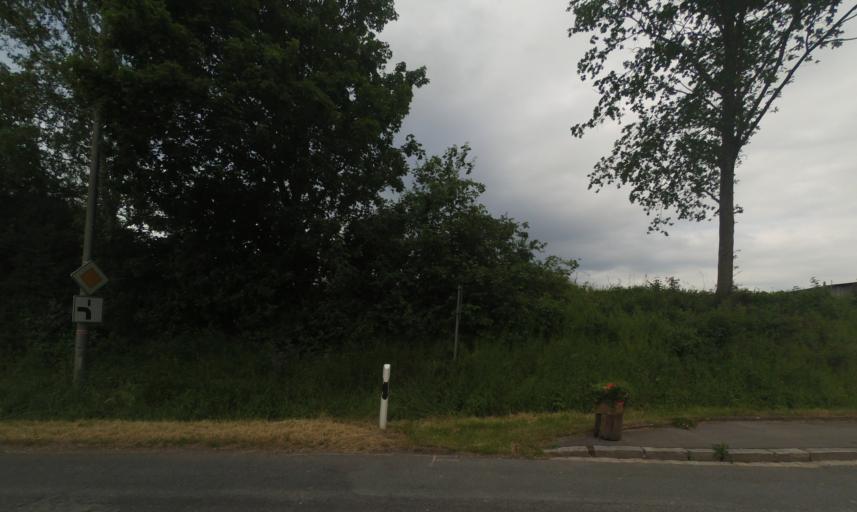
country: DE
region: Bavaria
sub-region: Regierungsbezirk Mittelfranken
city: Markt Taschendorf
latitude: 49.6986
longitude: 10.5836
